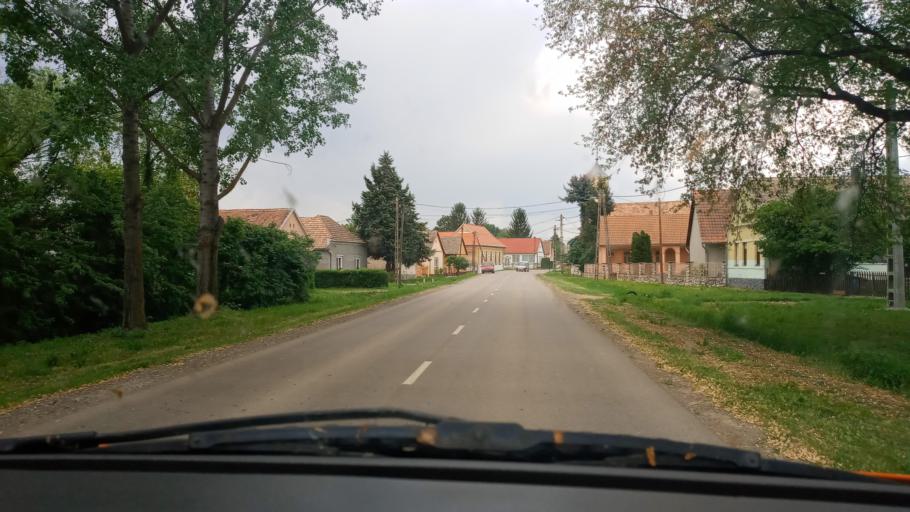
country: HU
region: Baranya
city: Villany
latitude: 45.8448
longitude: 18.4878
